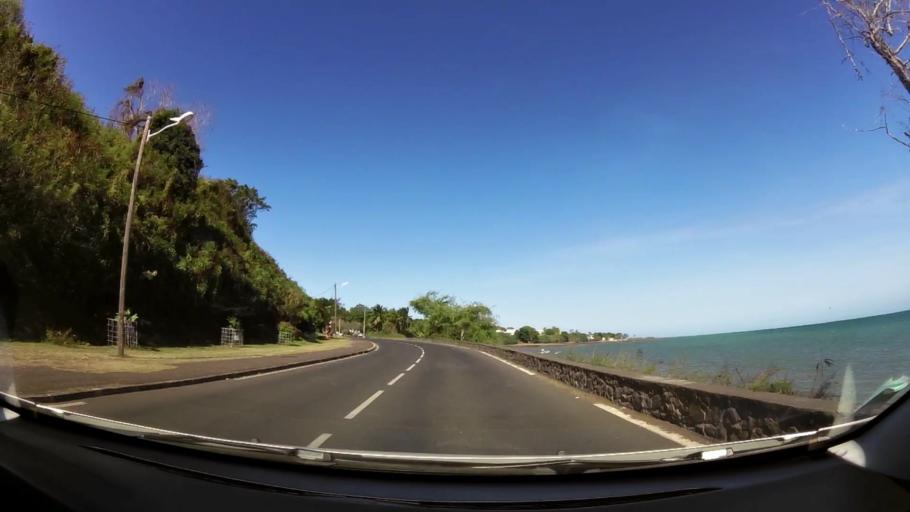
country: YT
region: Pamandzi
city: Pamandzi
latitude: -12.7920
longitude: 45.2693
